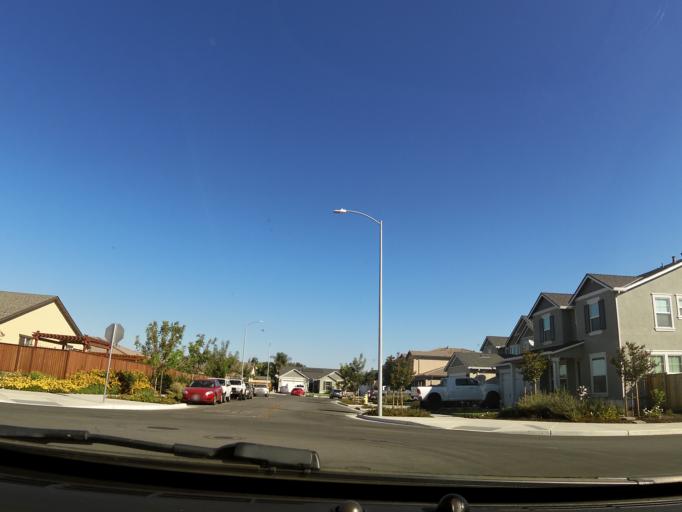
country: US
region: California
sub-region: San Benito County
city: Hollister
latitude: 36.8316
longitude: -121.3975
